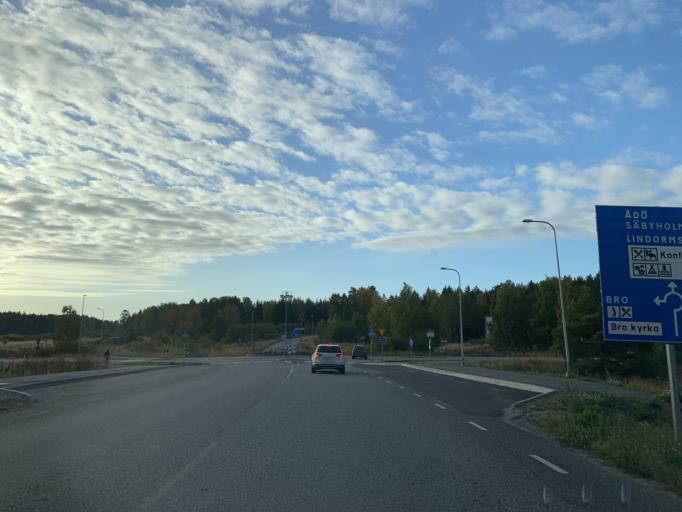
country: SE
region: Stockholm
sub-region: Upplands-Bro Kommun
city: Bro
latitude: 59.5137
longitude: 17.6152
